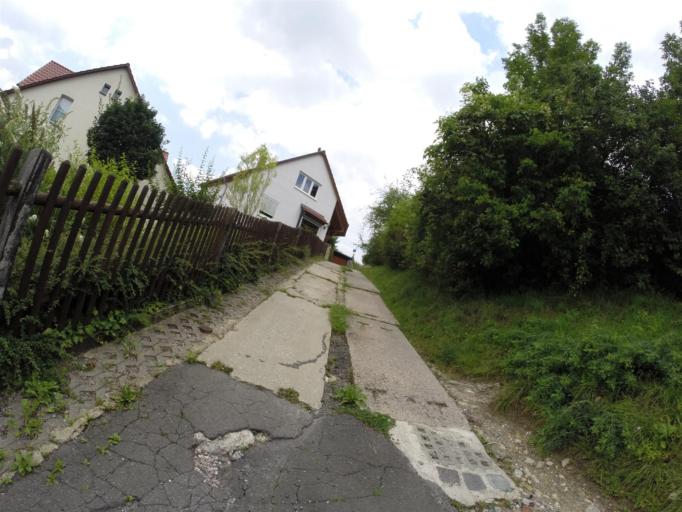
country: DE
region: Thuringia
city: Jena
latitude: 50.9301
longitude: 11.6080
